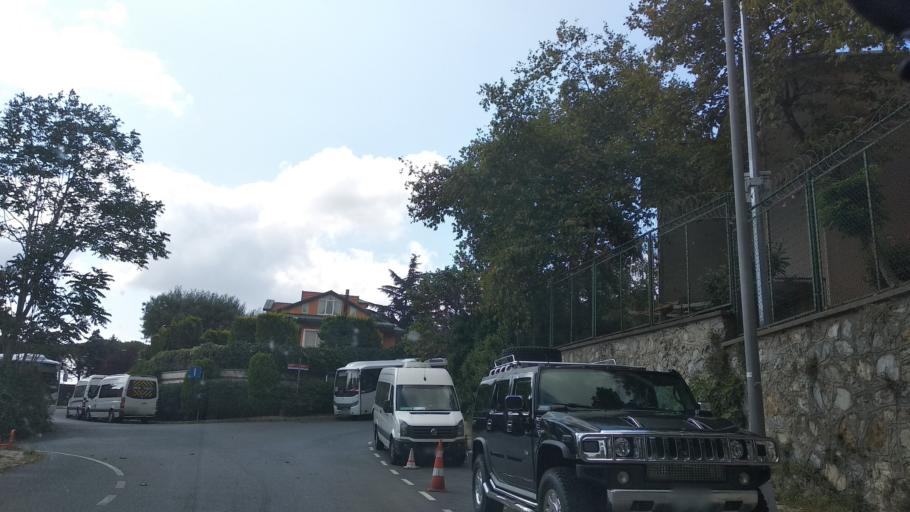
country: TR
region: Istanbul
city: Sisli
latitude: 41.0838
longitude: 29.0406
